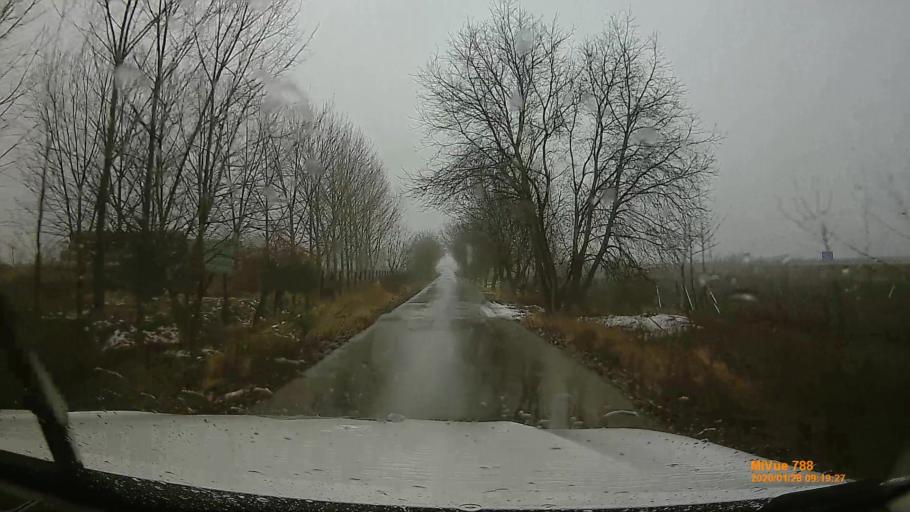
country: HU
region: Pest
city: Pilis
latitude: 47.3031
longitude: 19.5638
